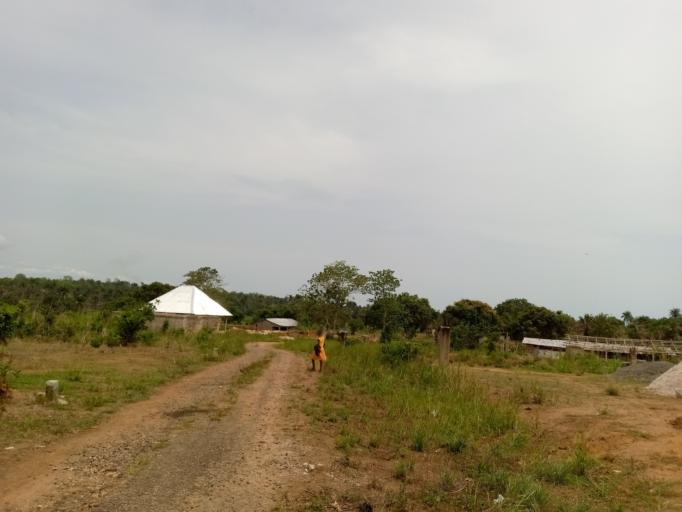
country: SL
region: Western Area
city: Waterloo
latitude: 8.3269
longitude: -13.0082
